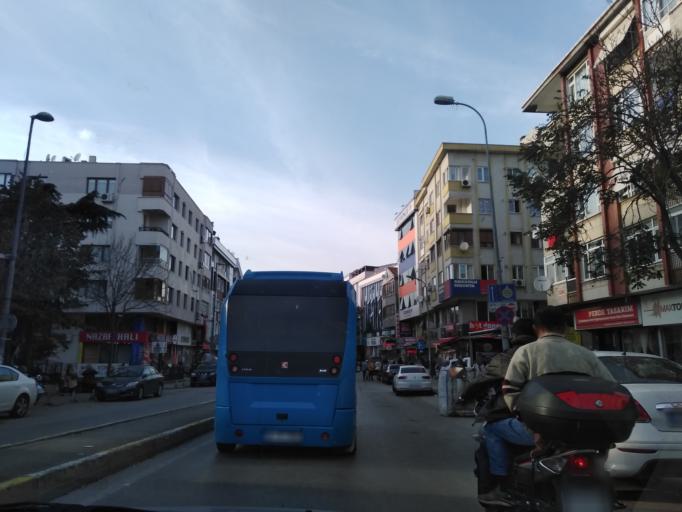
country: TR
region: Istanbul
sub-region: Atasehir
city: Atasehir
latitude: 40.9498
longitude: 29.1049
